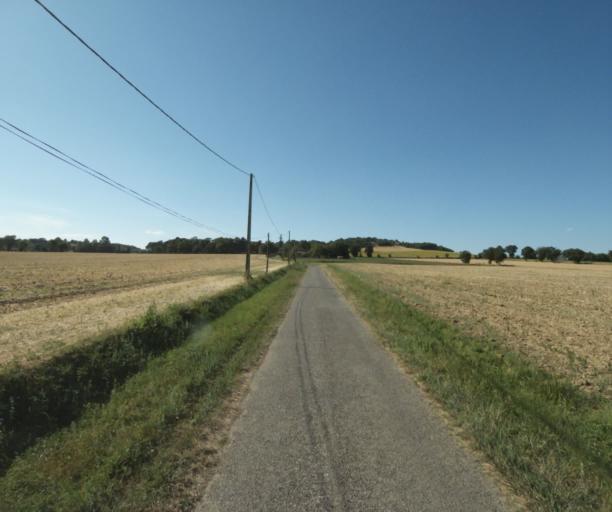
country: FR
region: Midi-Pyrenees
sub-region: Departement de la Haute-Garonne
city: Revel
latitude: 43.4918
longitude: 1.9441
